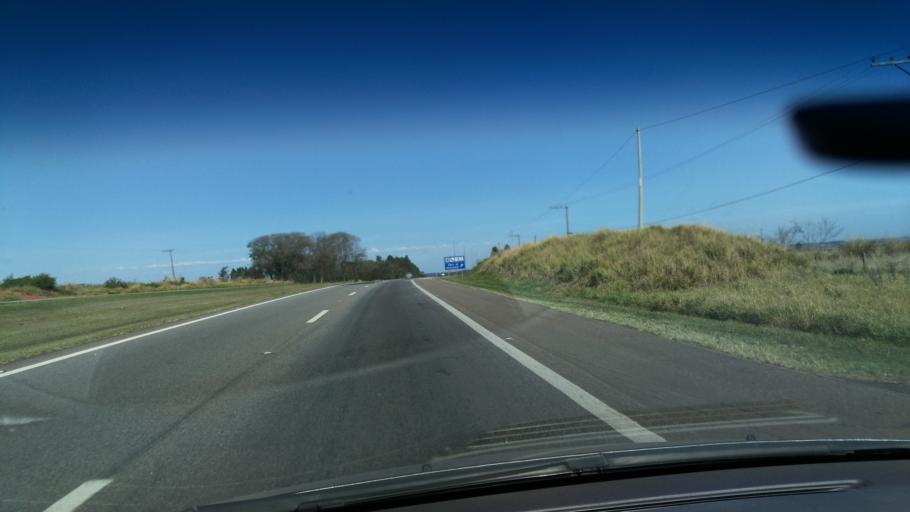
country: BR
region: Sao Paulo
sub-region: Mogi-Mirim
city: Mogi Mirim
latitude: -22.5233
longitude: -46.9918
